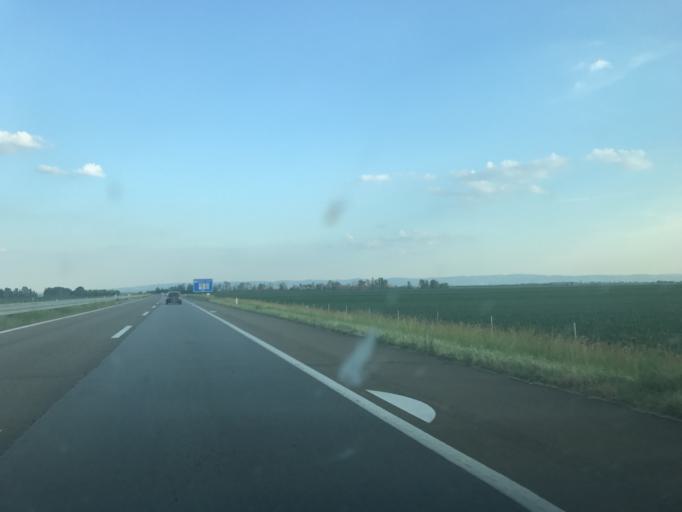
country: RS
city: Kisac
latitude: 45.3519
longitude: 19.7584
